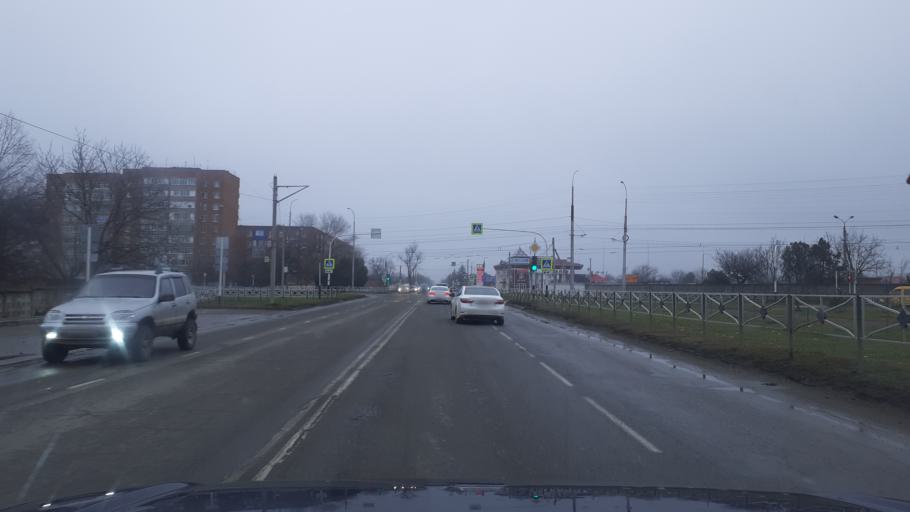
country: RU
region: Adygeya
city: Maykop
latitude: 44.6219
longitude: 40.0665
